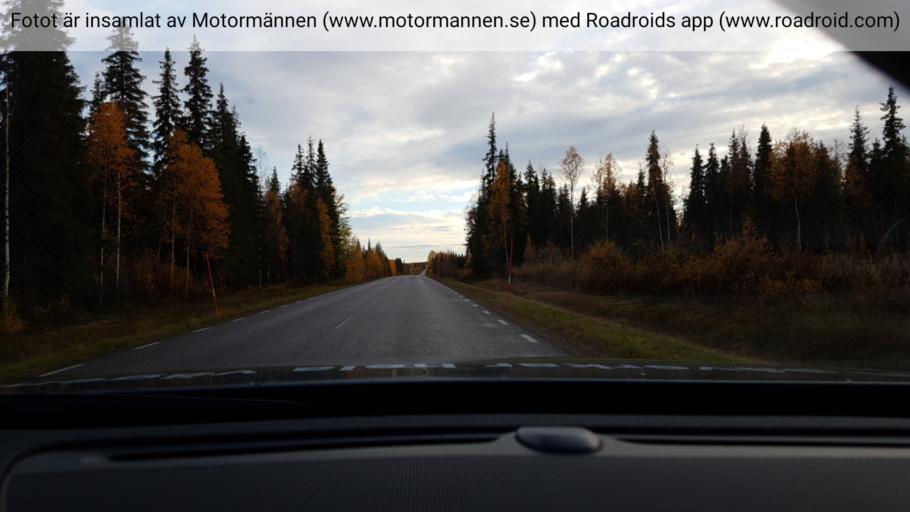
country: SE
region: Norrbotten
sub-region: Overkalix Kommun
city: OEverkalix
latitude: 66.9020
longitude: 22.7748
